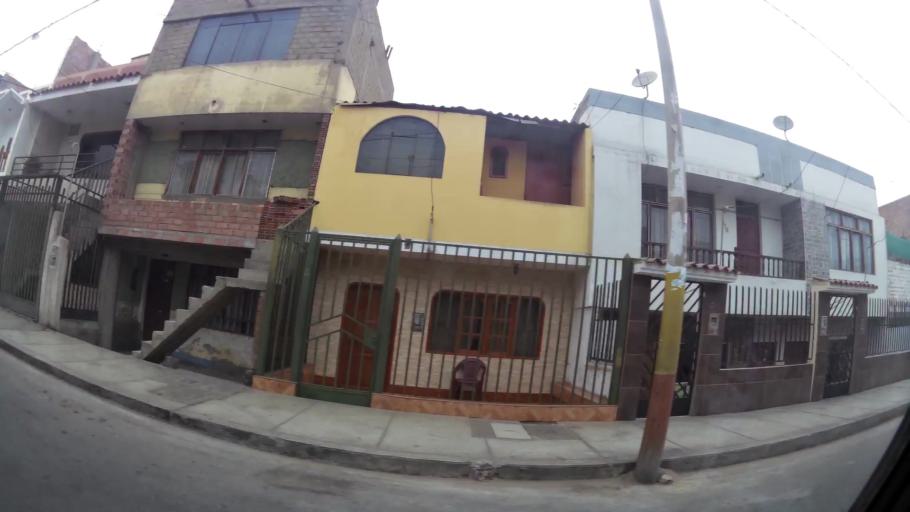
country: PE
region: Ancash
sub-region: Provincia de Santa
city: Chimbote
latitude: -9.0652
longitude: -78.5864
